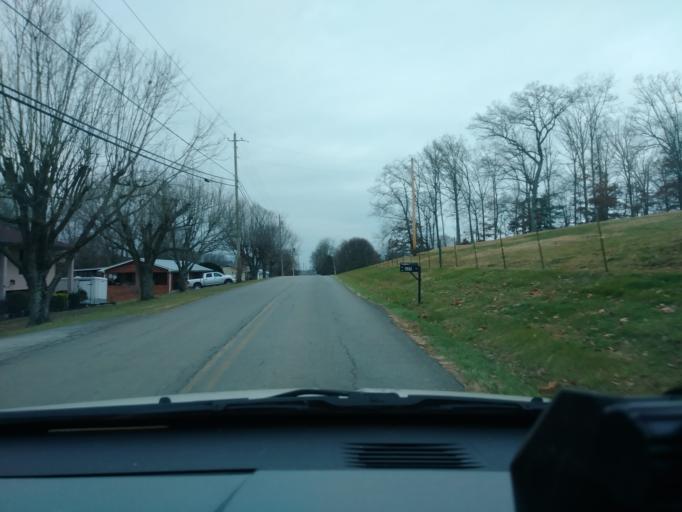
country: US
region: Tennessee
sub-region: Greene County
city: Greeneville
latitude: 36.1068
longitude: -82.8865
